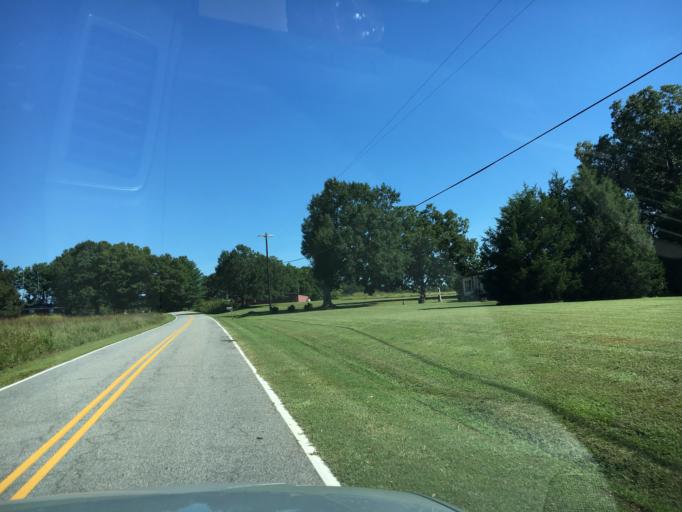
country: US
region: South Carolina
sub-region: Greenville County
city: Five Forks
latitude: 34.8505
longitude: -82.1565
